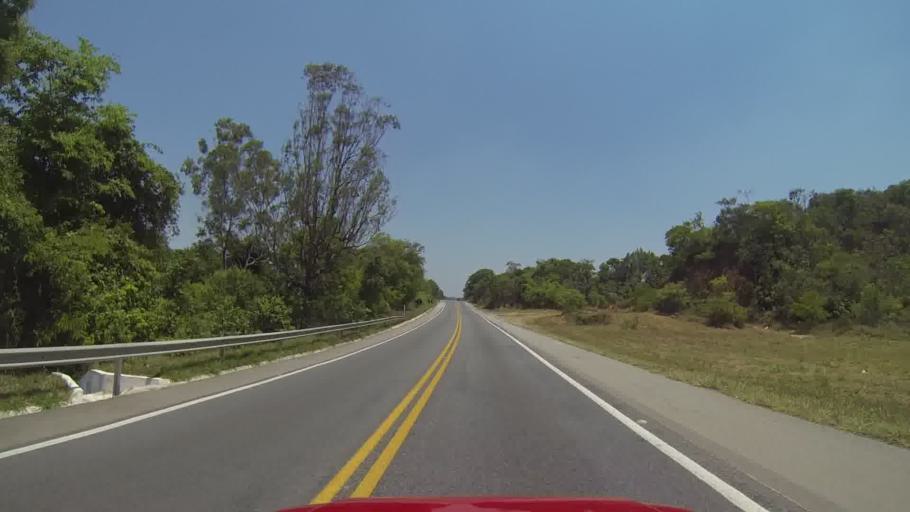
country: BR
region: Minas Gerais
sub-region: Itapecerica
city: Itapecerica
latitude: -20.2805
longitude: -45.1347
